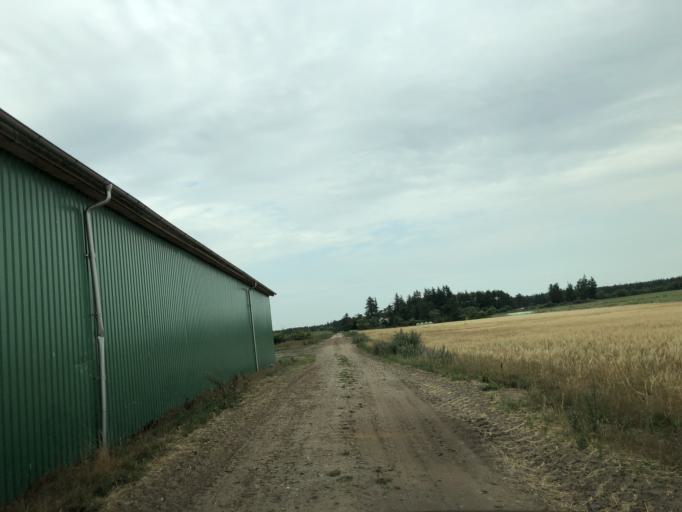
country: DK
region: Central Jutland
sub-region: Holstebro Kommune
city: Ulfborg
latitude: 56.2339
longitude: 8.3580
